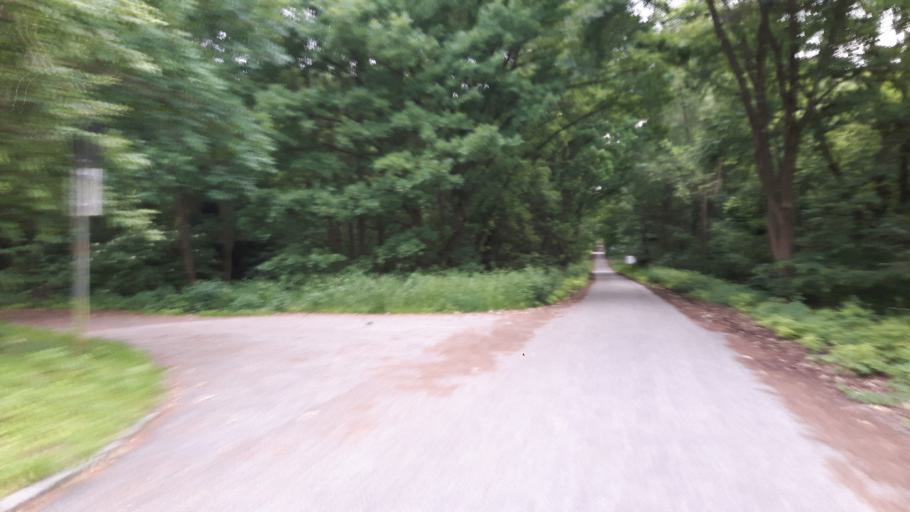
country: PL
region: West Pomeranian Voivodeship
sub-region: Powiat gryfinski
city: Widuchowa
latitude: 53.1326
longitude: 14.3482
